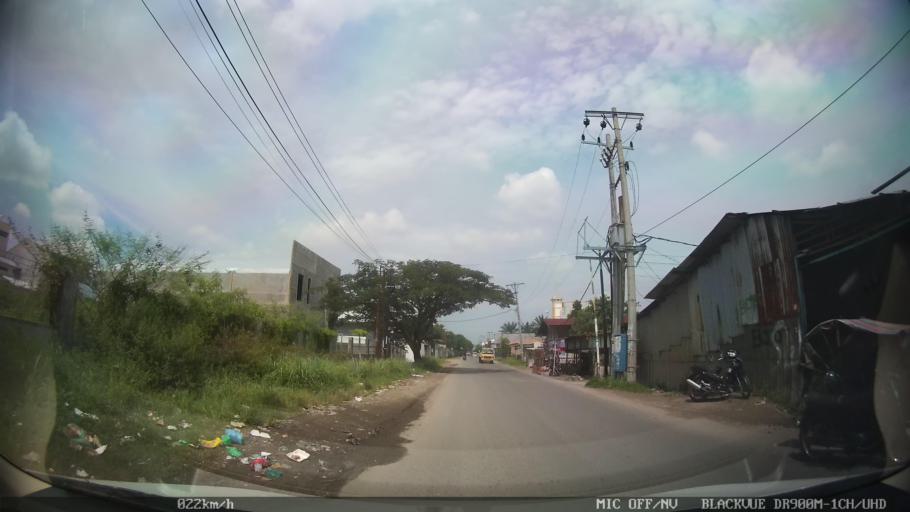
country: ID
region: North Sumatra
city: Medan
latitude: 3.6426
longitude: 98.6863
